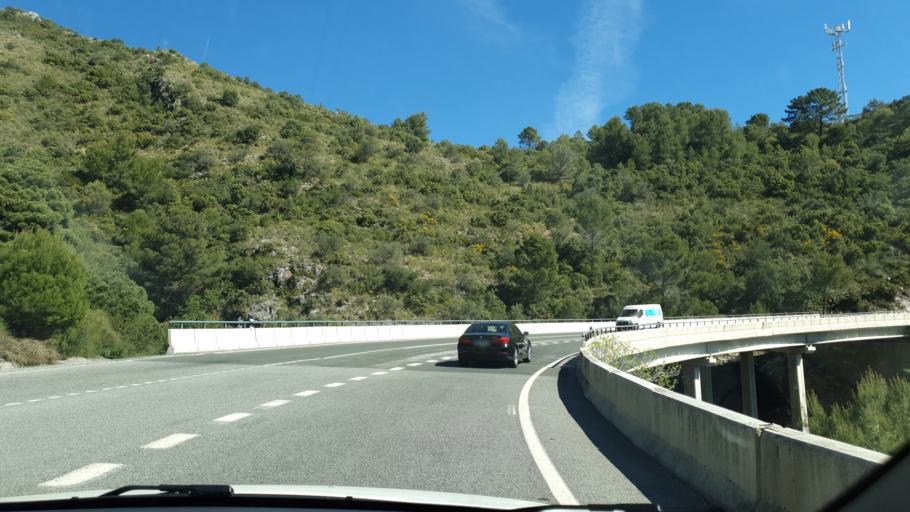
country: ES
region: Andalusia
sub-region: Provincia de Malaga
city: Ojen
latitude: 36.5580
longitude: -4.8643
